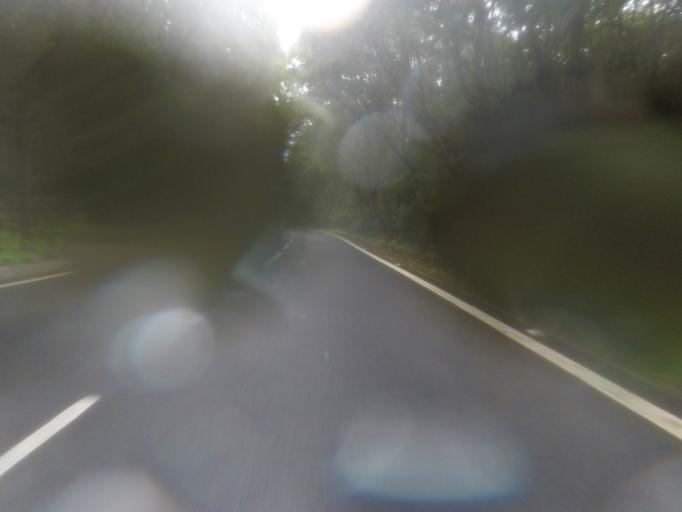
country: ES
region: Canary Islands
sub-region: Provincia de Santa Cruz de Tenerife
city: Vallehermosa
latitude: 28.1511
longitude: -17.2967
